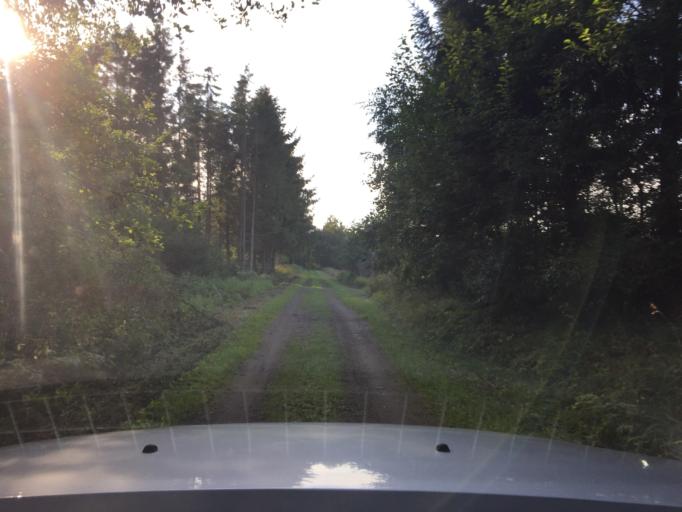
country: SE
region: Skane
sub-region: Hassleholms Kommun
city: Sosdala
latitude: 56.0156
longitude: 13.7239
